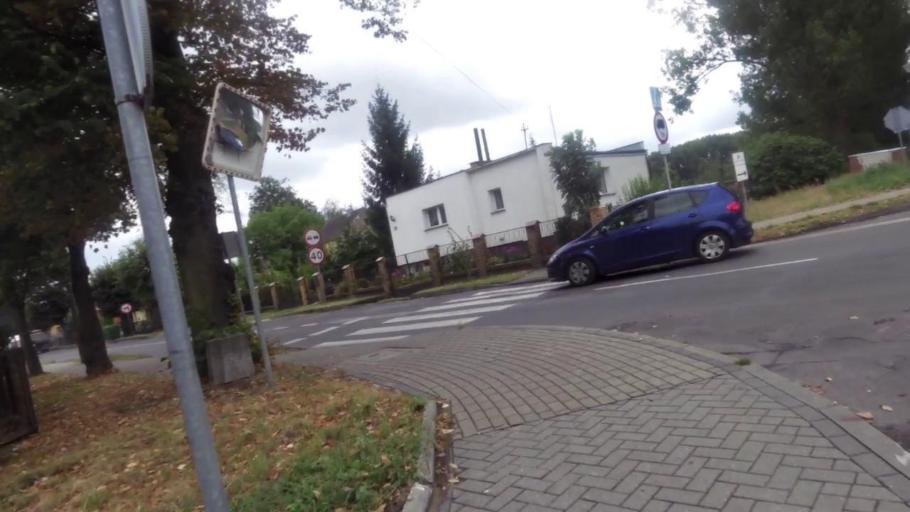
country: PL
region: Lubusz
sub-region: Powiat gorzowski
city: Kostrzyn nad Odra
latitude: 52.5995
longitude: 14.6345
